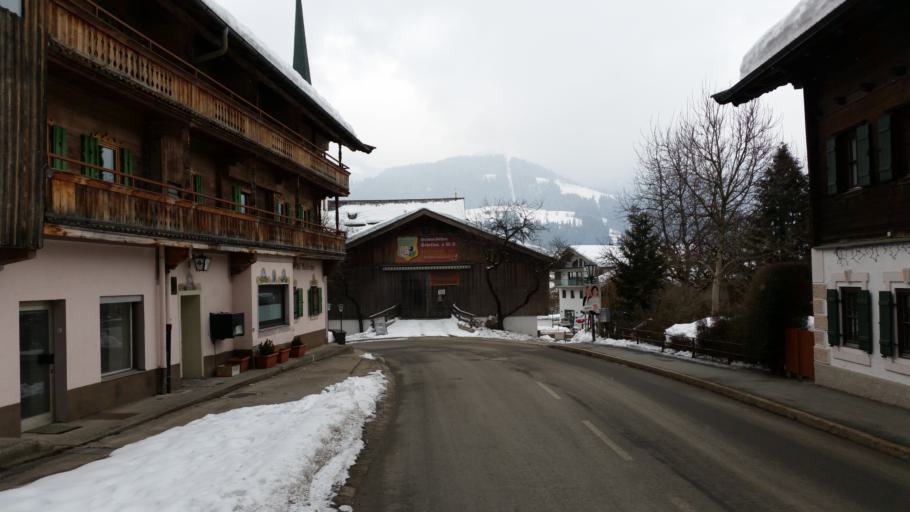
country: AT
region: Tyrol
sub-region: Politischer Bezirk Kufstein
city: Scheffau am Wilden Kaiser
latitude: 47.5296
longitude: 12.2494
